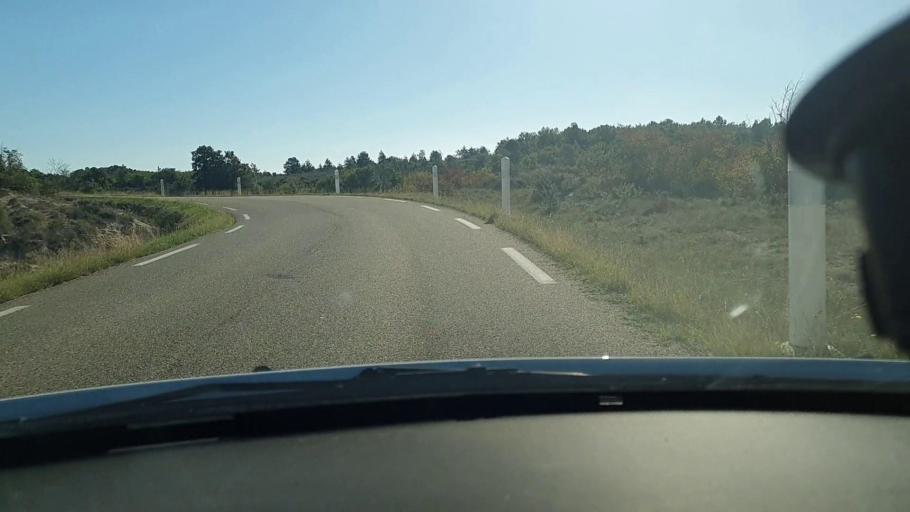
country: FR
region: Languedoc-Roussillon
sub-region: Departement du Gard
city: Goudargues
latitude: 44.2831
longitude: 4.4586
